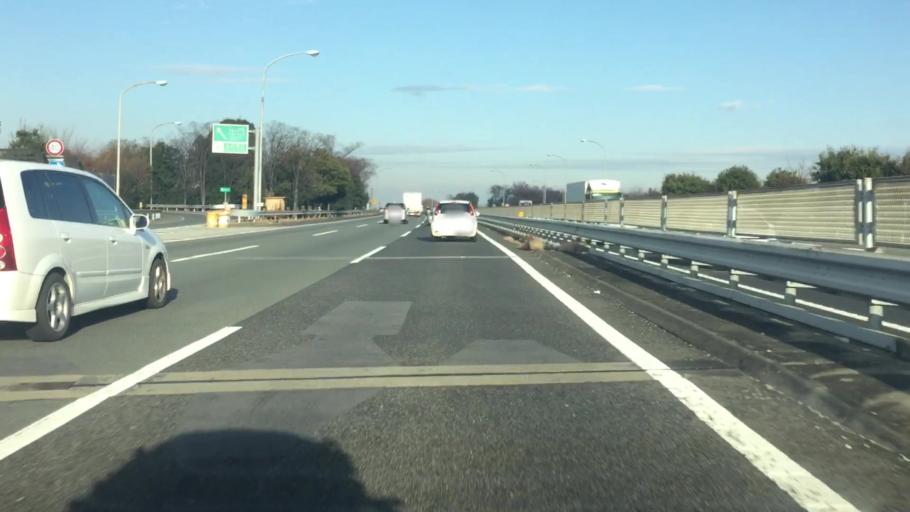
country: JP
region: Saitama
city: Honjo
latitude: 36.2164
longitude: 139.1658
